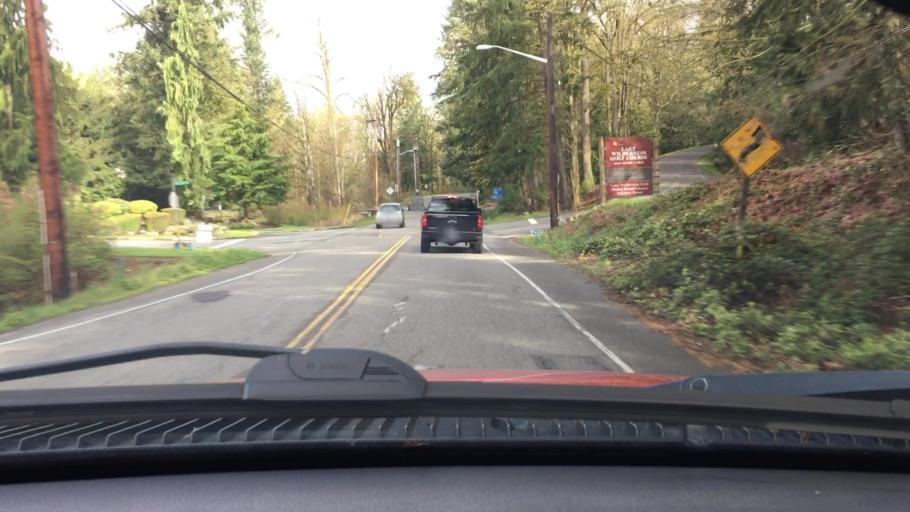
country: US
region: Washington
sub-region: King County
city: Maple Valley
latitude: 47.3734
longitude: -122.0482
